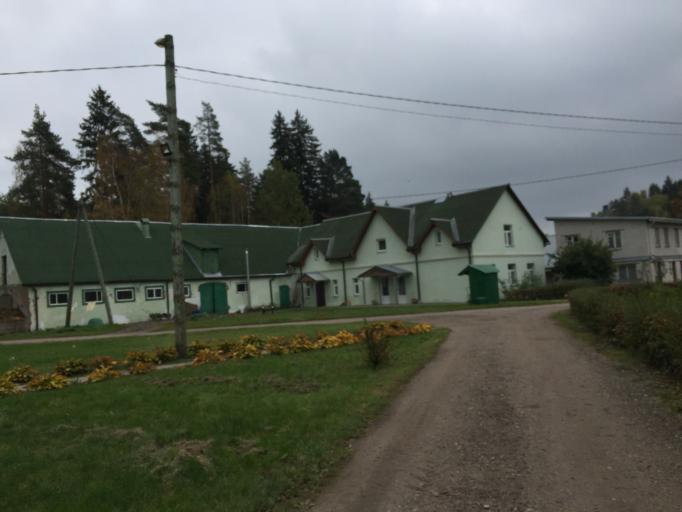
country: LV
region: Jelgava
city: Jelgava
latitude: 56.7343
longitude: 23.6952
